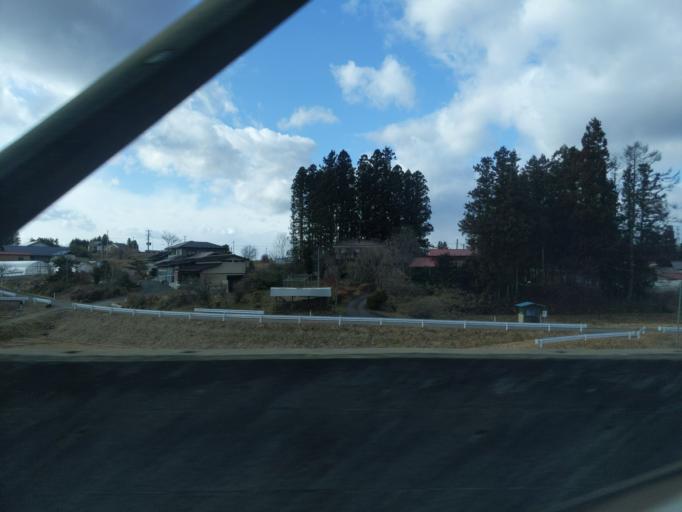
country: JP
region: Iwate
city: Ichinoseki
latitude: 38.8448
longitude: 141.1096
